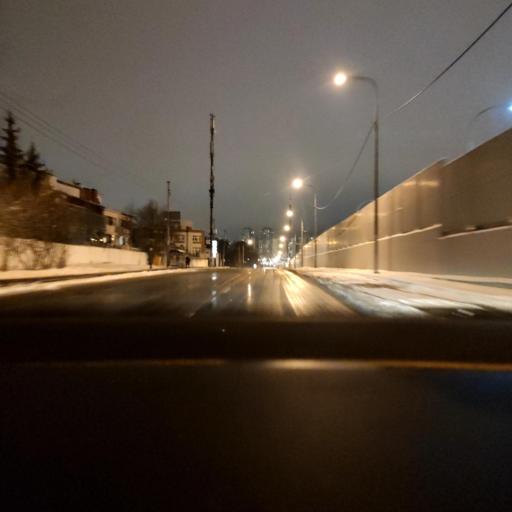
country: RU
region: Moskovskaya
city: Pavshino
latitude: 55.8624
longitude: 37.3625
